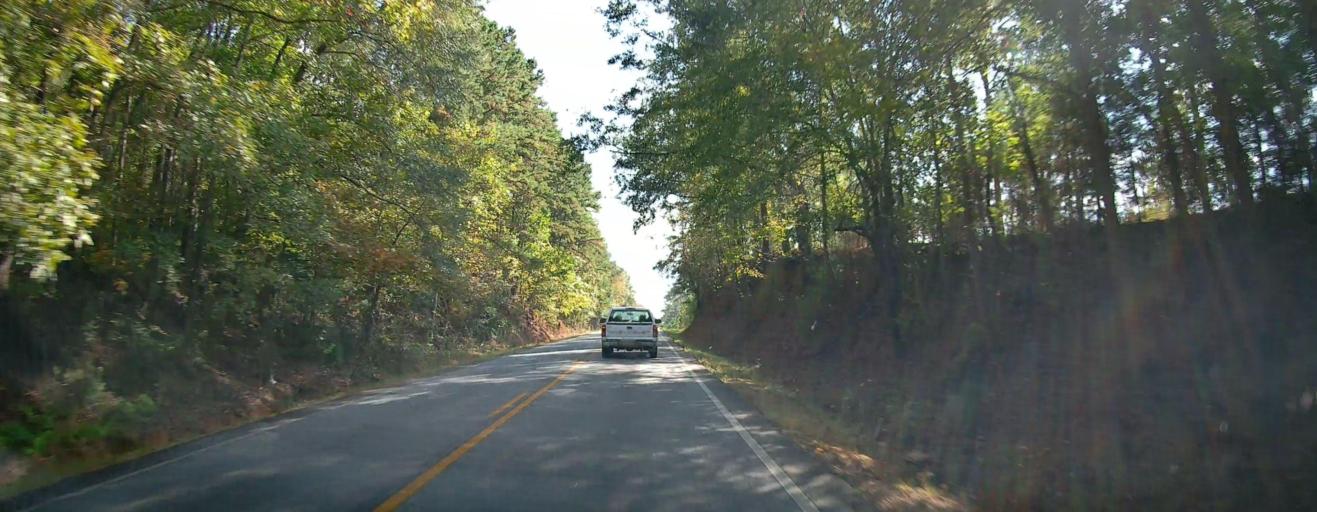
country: US
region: Georgia
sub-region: Thomas County
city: Thomasville
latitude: 30.9028
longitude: -84.0062
